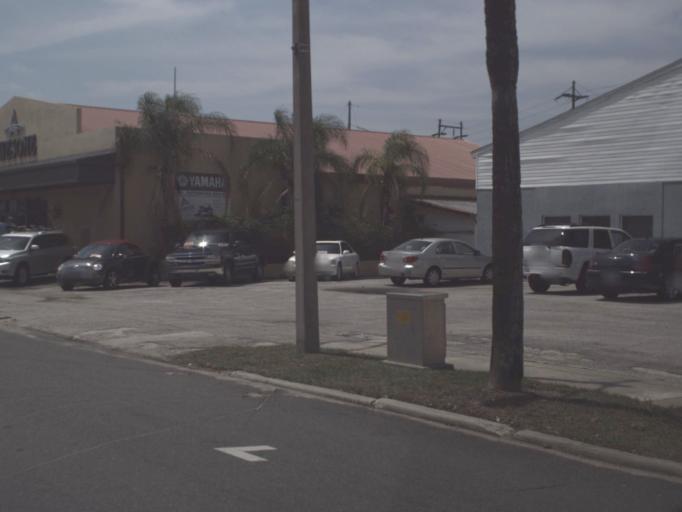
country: US
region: Florida
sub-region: Lake County
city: Eustis
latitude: 28.8516
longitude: -81.6856
